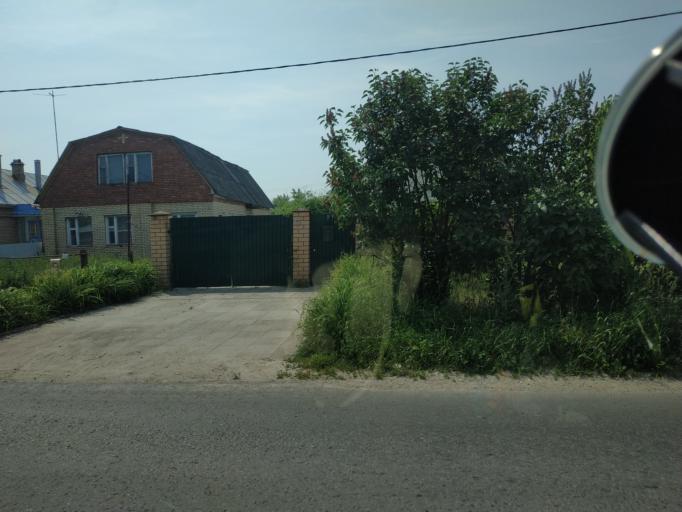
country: RU
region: Moskovskaya
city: Malyshevo
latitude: 55.5007
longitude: 38.3362
